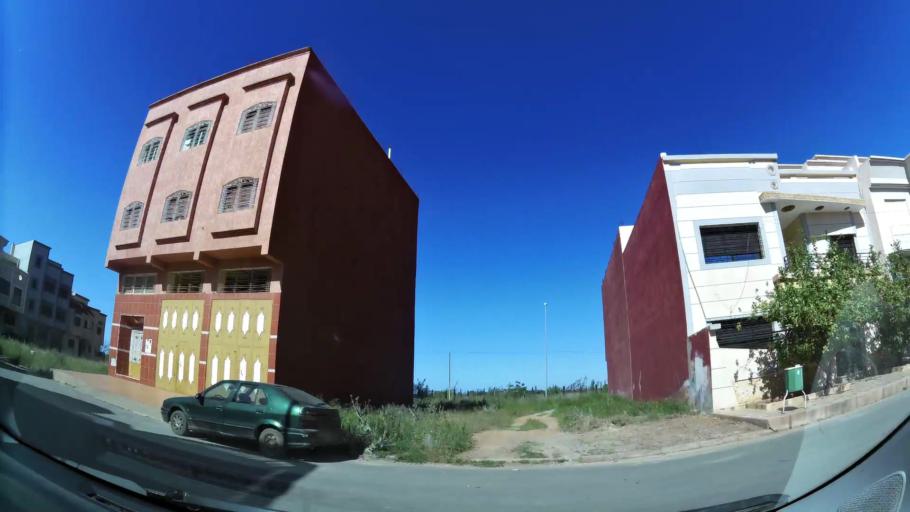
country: MA
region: Oriental
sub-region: Berkane-Taourirt
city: Berkane
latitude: 34.9464
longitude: -2.3348
